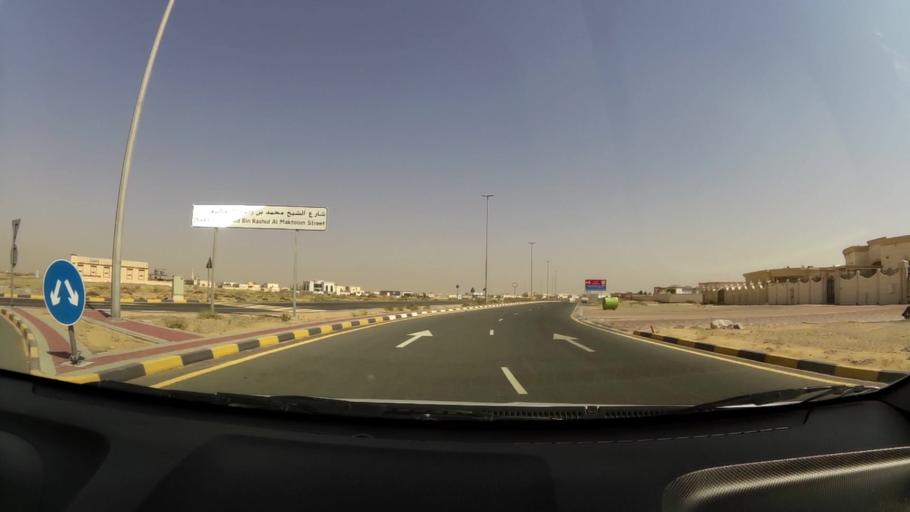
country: AE
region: Umm al Qaywayn
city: Umm al Qaywayn
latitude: 25.4785
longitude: 55.6041
